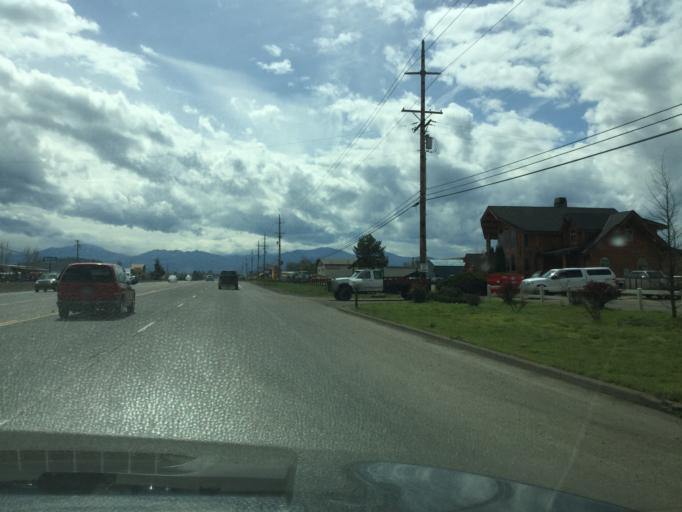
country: US
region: Oregon
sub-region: Jackson County
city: White City
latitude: 42.4119
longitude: -122.8562
